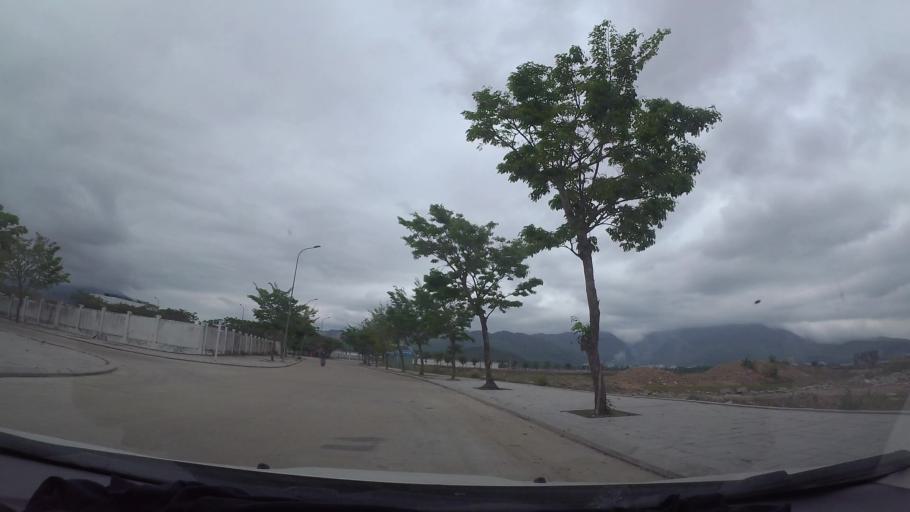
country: VN
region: Da Nang
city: Lien Chieu
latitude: 16.1058
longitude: 108.1215
